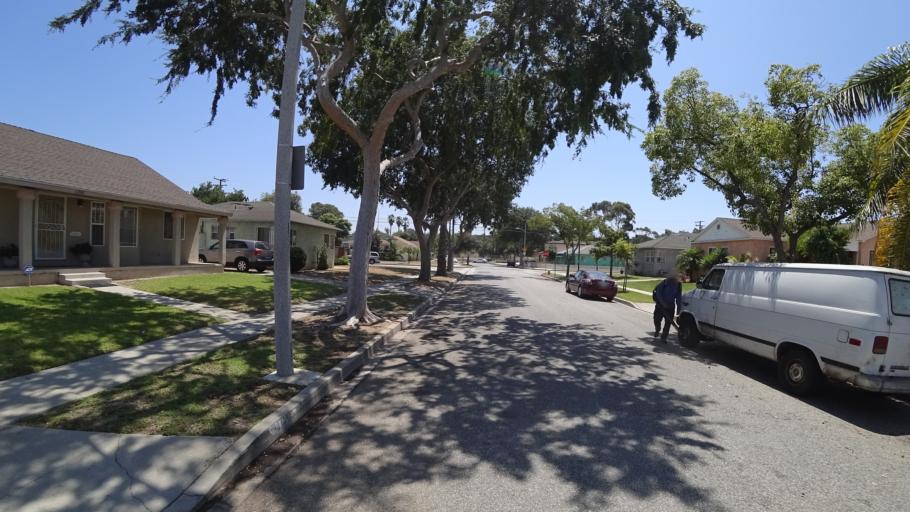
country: US
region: California
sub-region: Los Angeles County
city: West Athens
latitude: 33.9268
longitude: -118.3285
